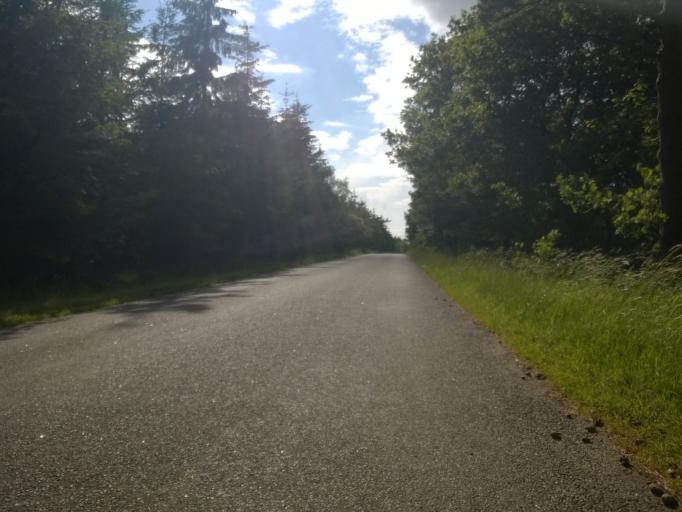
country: DK
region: Central Jutland
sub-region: Holstebro Kommune
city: Vinderup
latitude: 56.4806
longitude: 8.8607
